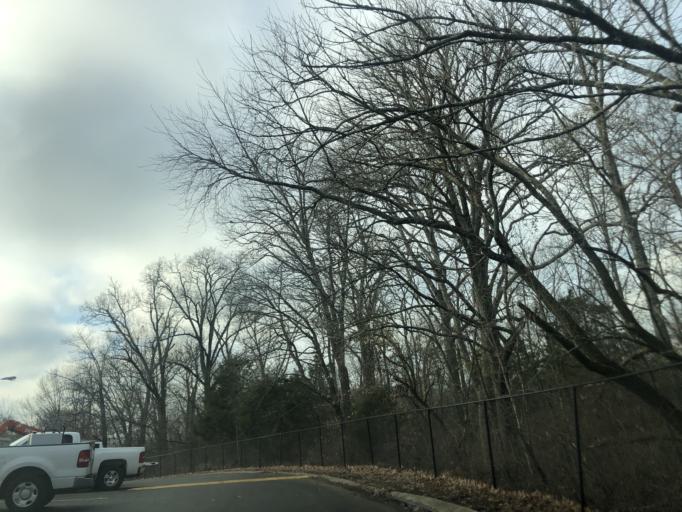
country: US
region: Tennessee
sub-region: Davidson County
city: Nashville
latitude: 36.2155
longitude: -86.7927
